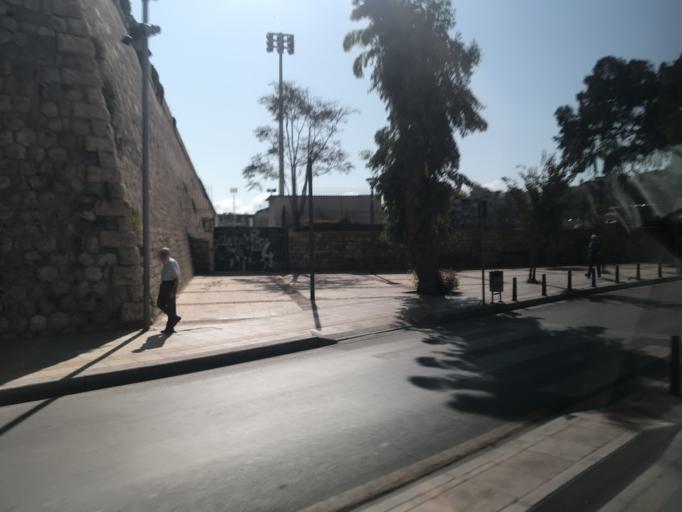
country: GR
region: Crete
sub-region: Nomos Irakleiou
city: Irakleion
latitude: 35.3369
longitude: 25.1249
